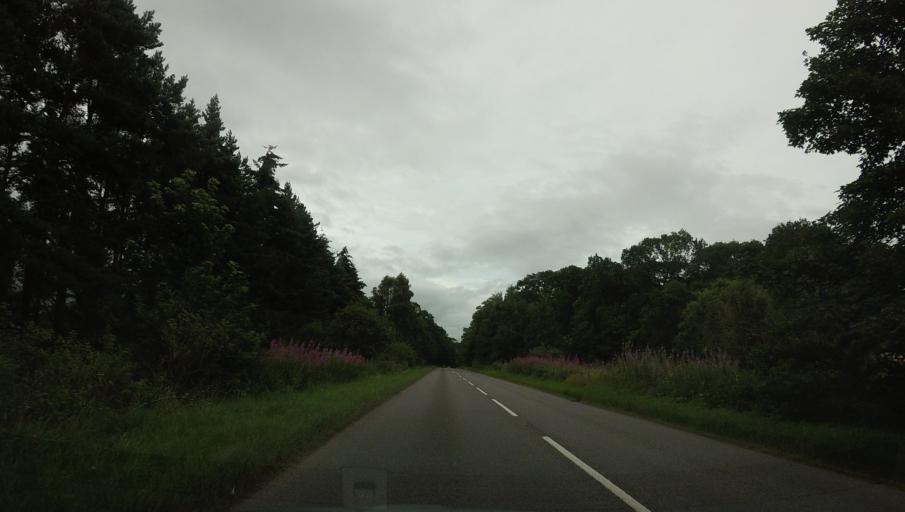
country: GB
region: Scotland
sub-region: Aberdeenshire
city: Aboyne
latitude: 57.0814
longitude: -2.7658
